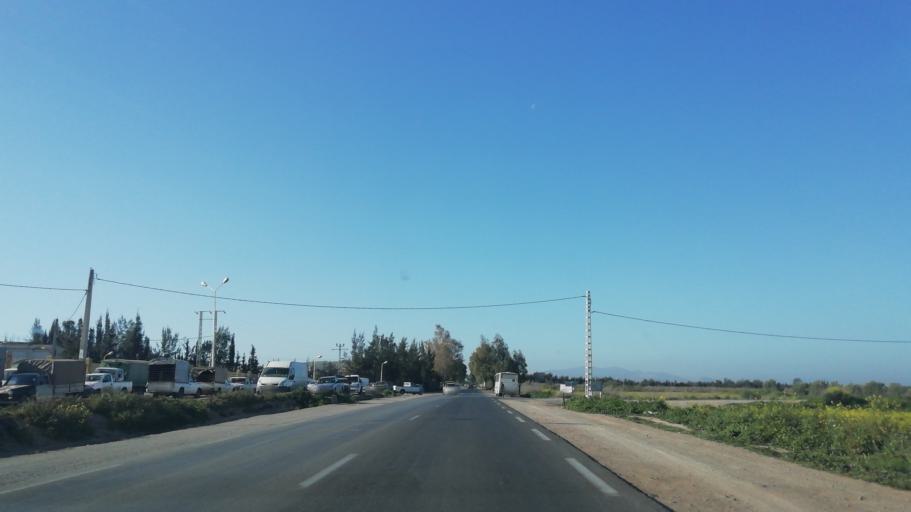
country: DZ
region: Mascara
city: Mascara
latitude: 35.6326
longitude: 0.1316
